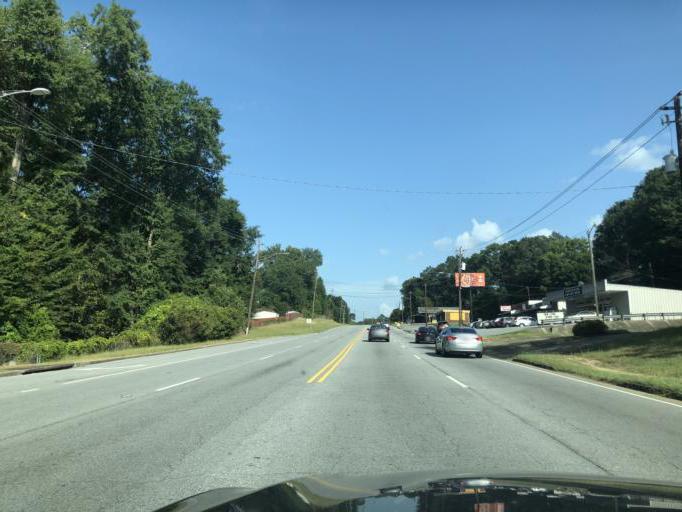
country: US
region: Georgia
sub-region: Muscogee County
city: Columbus
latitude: 32.4845
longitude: -84.9062
